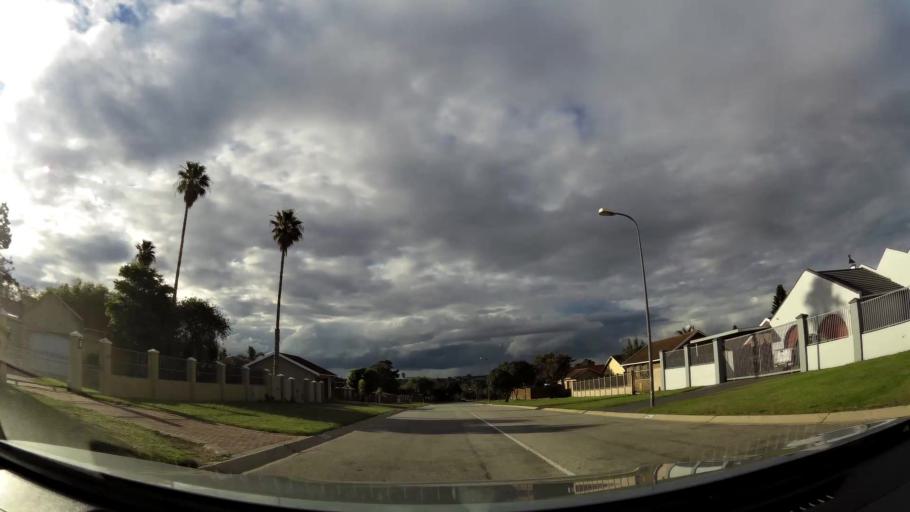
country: ZA
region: Eastern Cape
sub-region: Nelson Mandela Bay Metropolitan Municipality
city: Port Elizabeth
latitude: -33.9557
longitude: 25.4806
